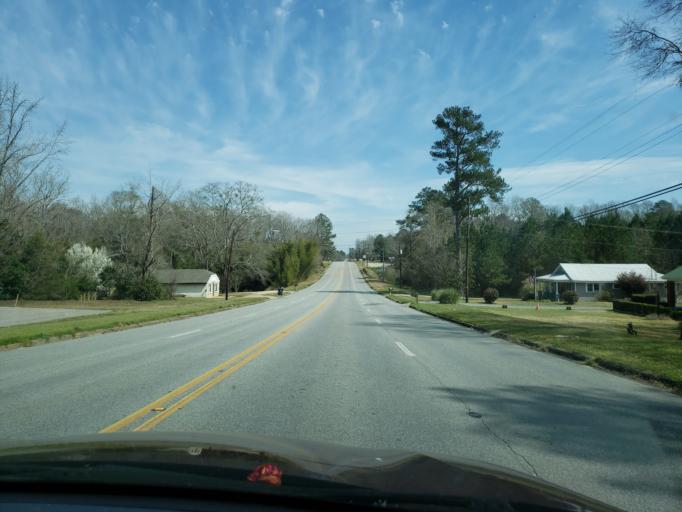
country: US
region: Alabama
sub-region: Elmore County
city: Tallassee
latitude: 32.5516
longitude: -85.8607
